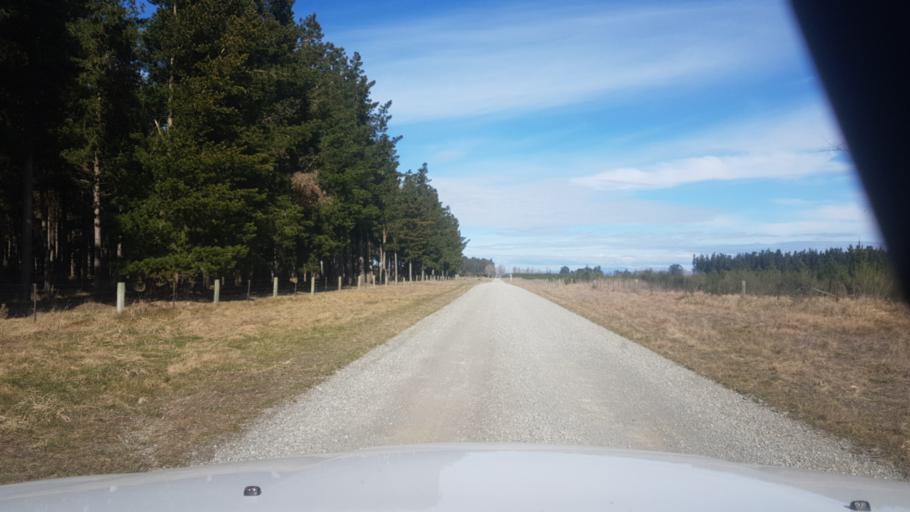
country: NZ
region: Canterbury
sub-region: Timaru District
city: Pleasant Point
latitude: -44.1294
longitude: 171.2805
